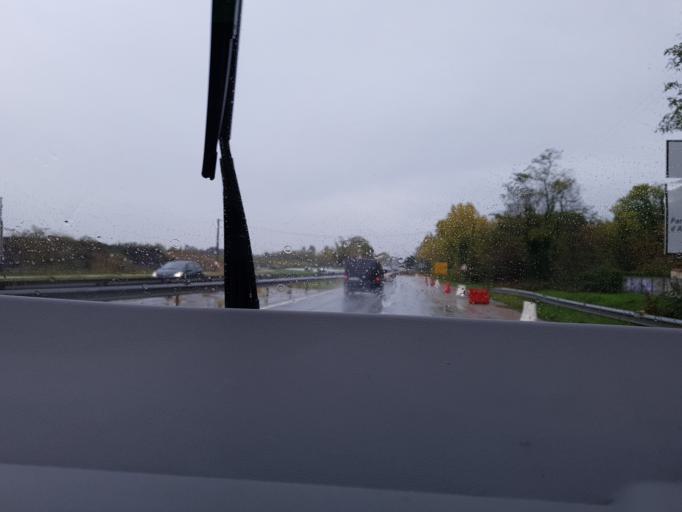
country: FR
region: Aquitaine
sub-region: Departement de la Gironde
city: Saint-Gervais
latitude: 45.0080
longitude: -0.4338
